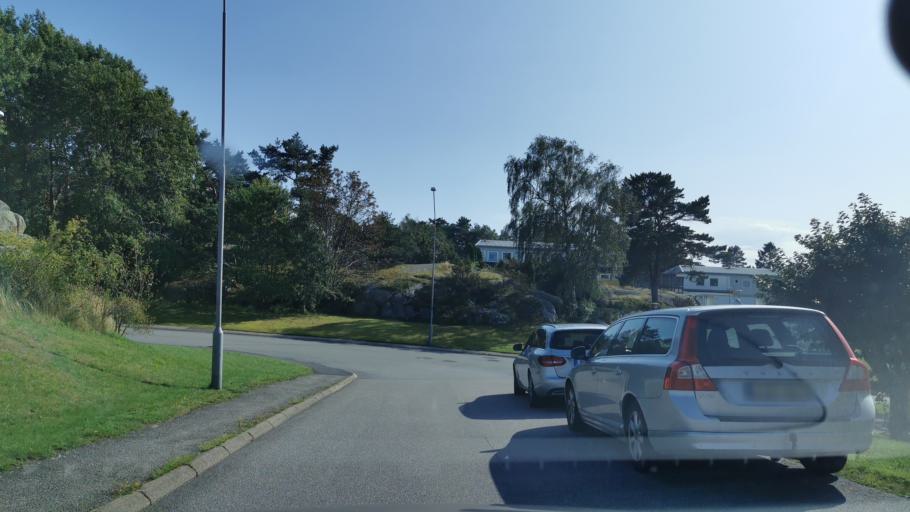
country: SE
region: Vaestra Goetaland
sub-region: Goteborg
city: Majorna
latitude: 57.6417
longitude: 11.9093
